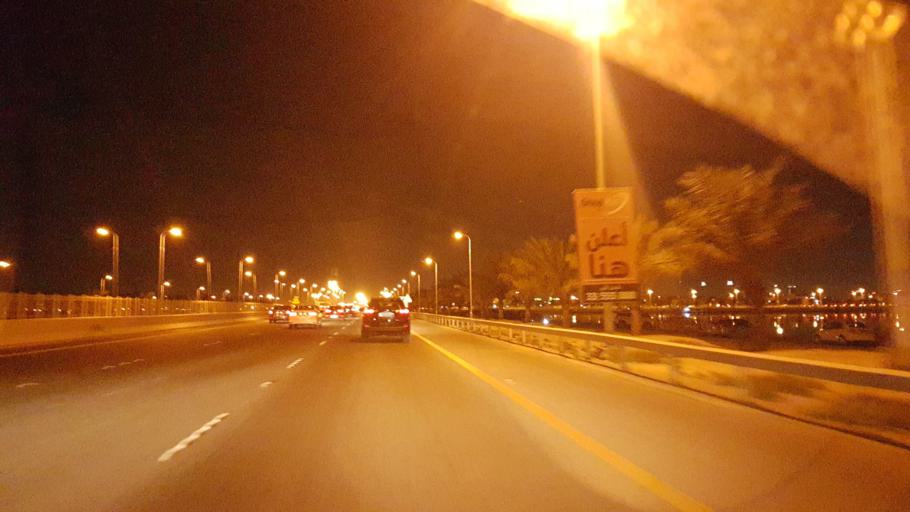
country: BH
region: Muharraq
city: Al Hadd
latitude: 26.2591
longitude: 50.6605
